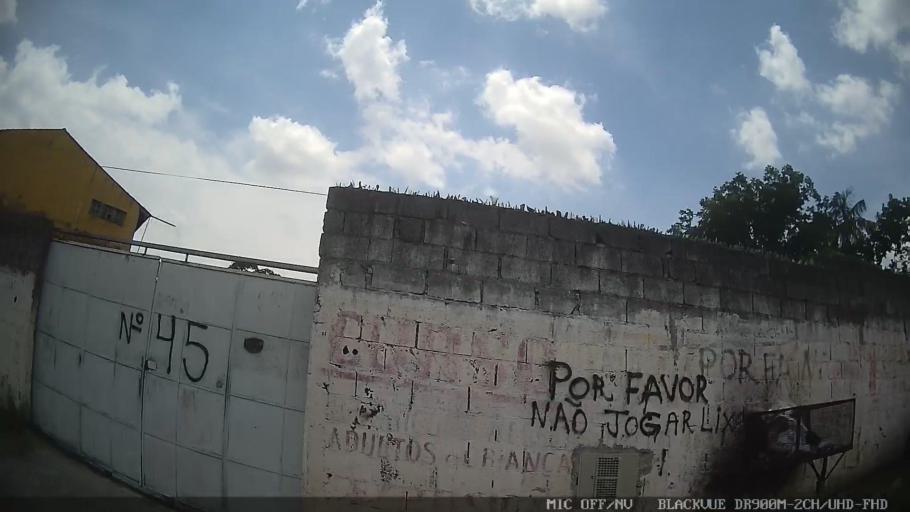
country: BR
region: Sao Paulo
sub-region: Ferraz De Vasconcelos
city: Ferraz de Vasconcelos
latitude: -23.5529
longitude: -46.3734
